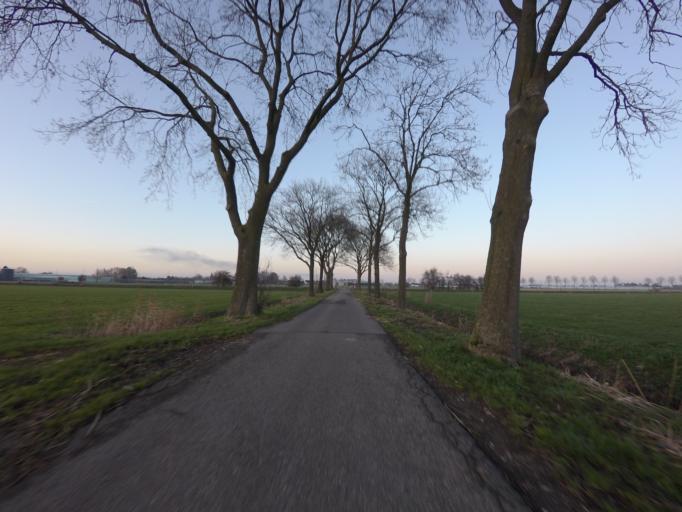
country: NL
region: Gelderland
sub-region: Gemeente Maasdriel
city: Hedel
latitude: 51.7690
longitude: 5.2251
